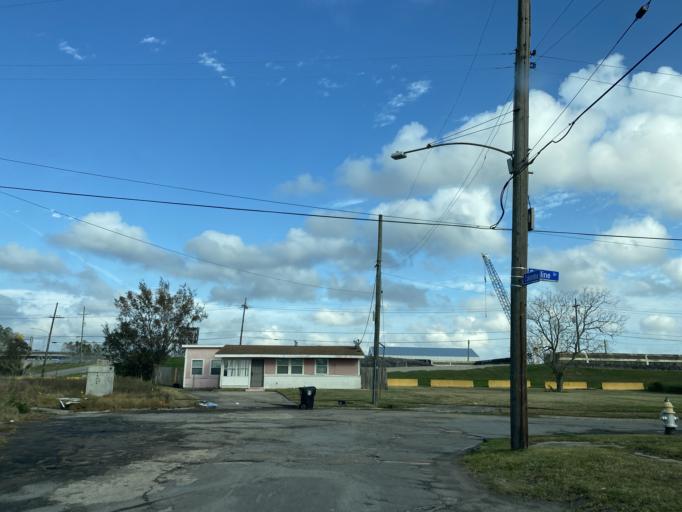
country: US
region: Louisiana
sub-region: Saint Bernard Parish
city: Arabi
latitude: 30.0296
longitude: -90.0382
